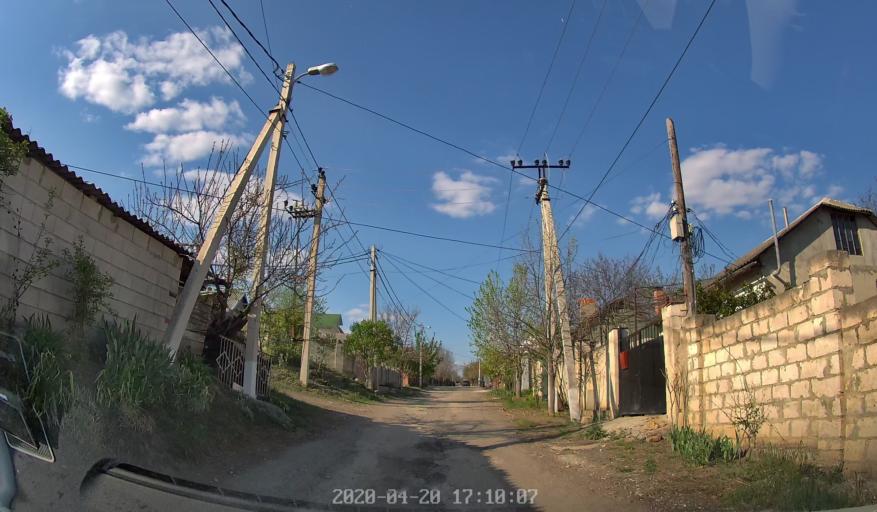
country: MD
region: Chisinau
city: Chisinau
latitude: 46.9613
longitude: 28.8405
